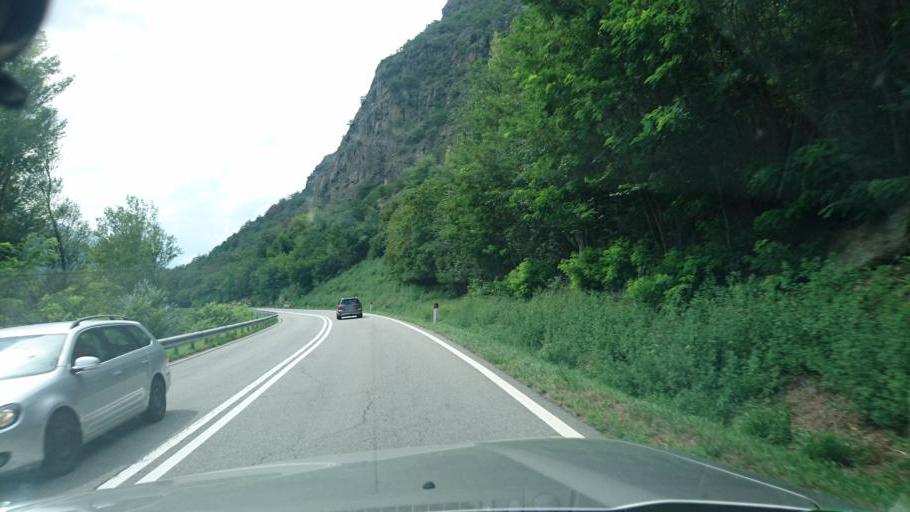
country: IT
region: Trentino-Alto Adige
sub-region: Bolzano
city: Laces
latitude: 46.6227
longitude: 10.8613
